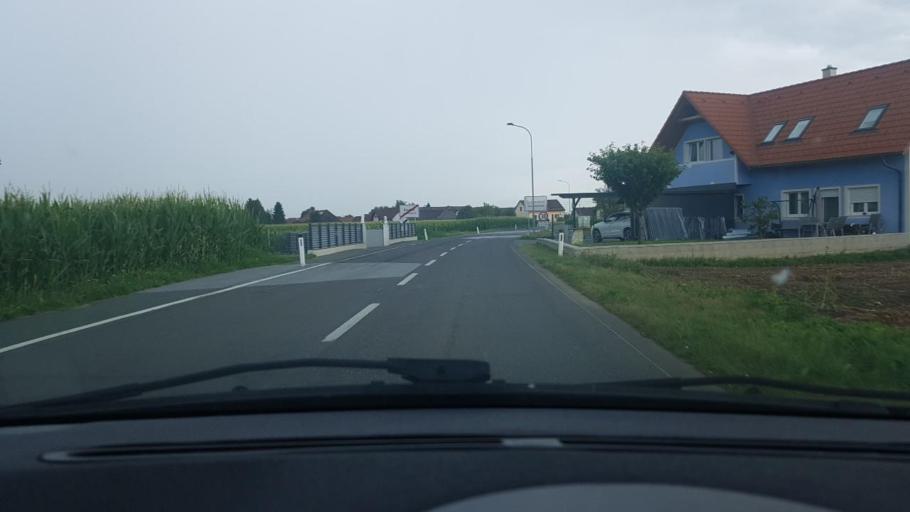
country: AT
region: Styria
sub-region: Politischer Bezirk Graz-Umgebung
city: Wundschuh
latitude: 46.9423
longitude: 15.4456
